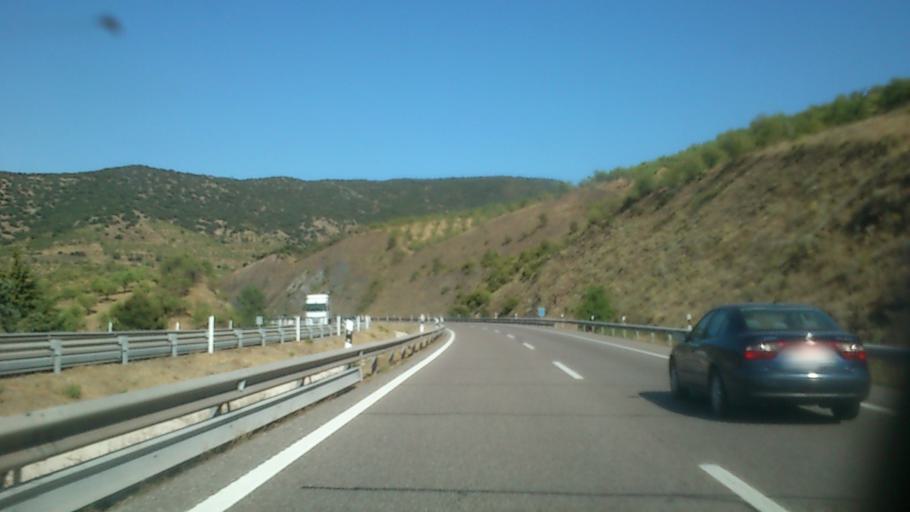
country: ES
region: Aragon
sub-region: Provincia de Zaragoza
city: Paracuellos de la Ribera
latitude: 41.4022
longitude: -1.5339
